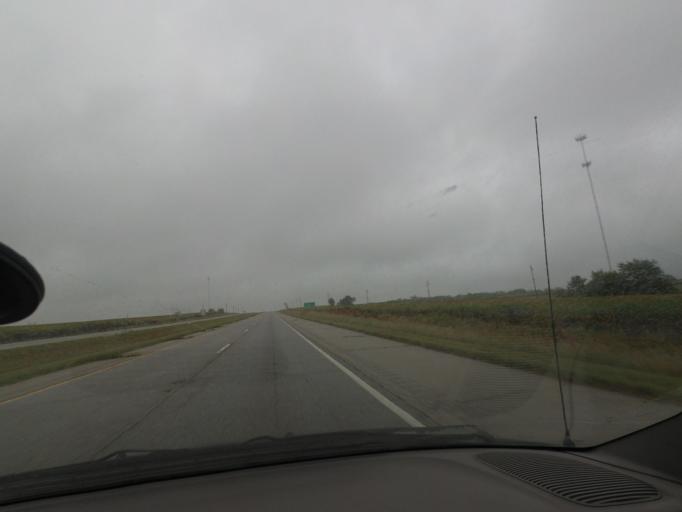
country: US
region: Illinois
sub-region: Pike County
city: Barry
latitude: 39.7003
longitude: -91.0246
